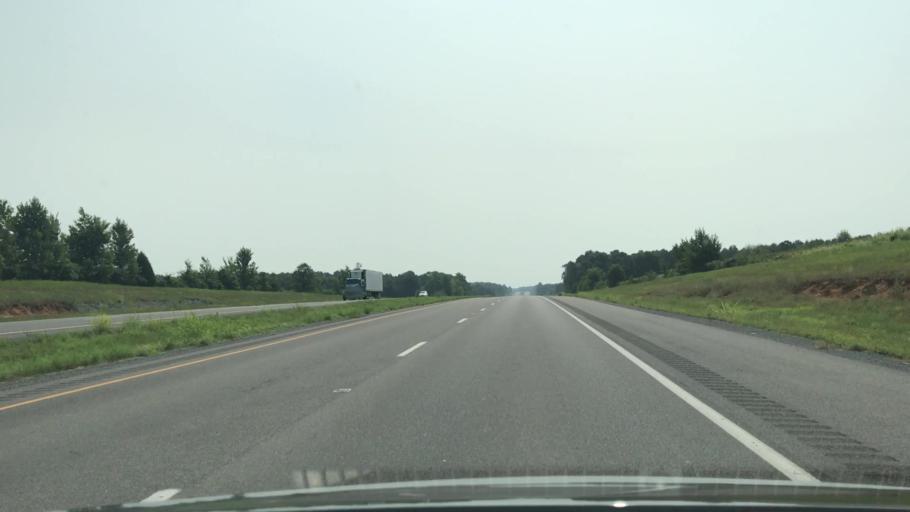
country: US
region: Kentucky
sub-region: Graves County
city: Mayfield
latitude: 36.6715
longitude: -88.5048
